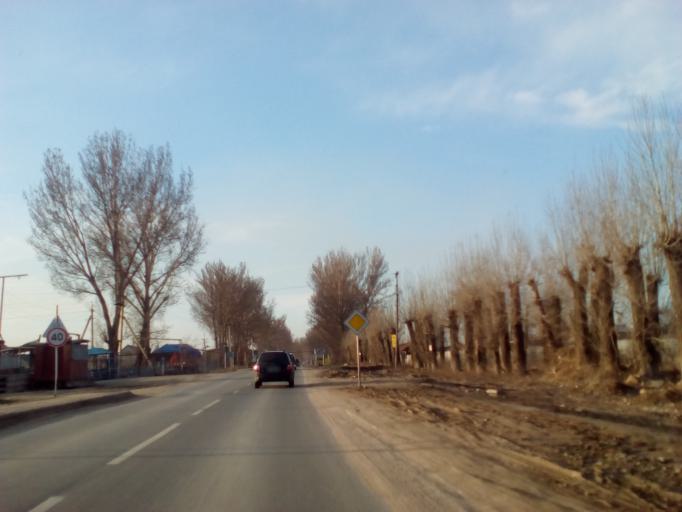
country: KZ
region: Almaty Oblysy
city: Burunday
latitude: 43.2460
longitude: 76.7858
